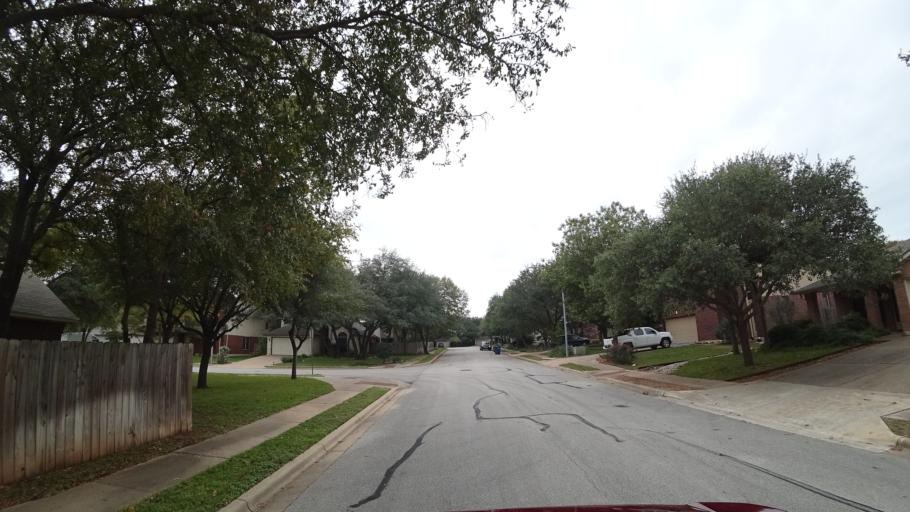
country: US
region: Texas
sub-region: Travis County
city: Wells Branch
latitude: 30.4290
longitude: -97.7183
